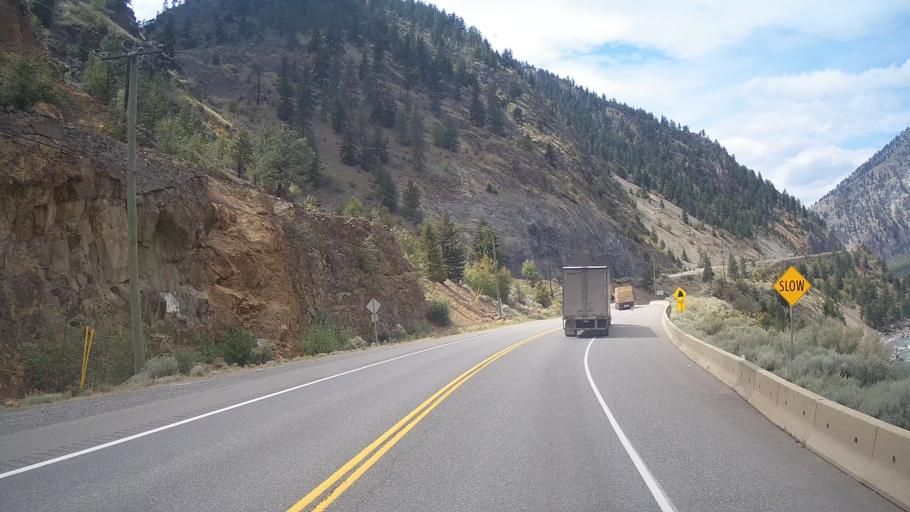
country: CA
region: British Columbia
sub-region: Thompson-Nicola Regional District
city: Ashcroft
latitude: 50.2546
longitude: -121.4427
